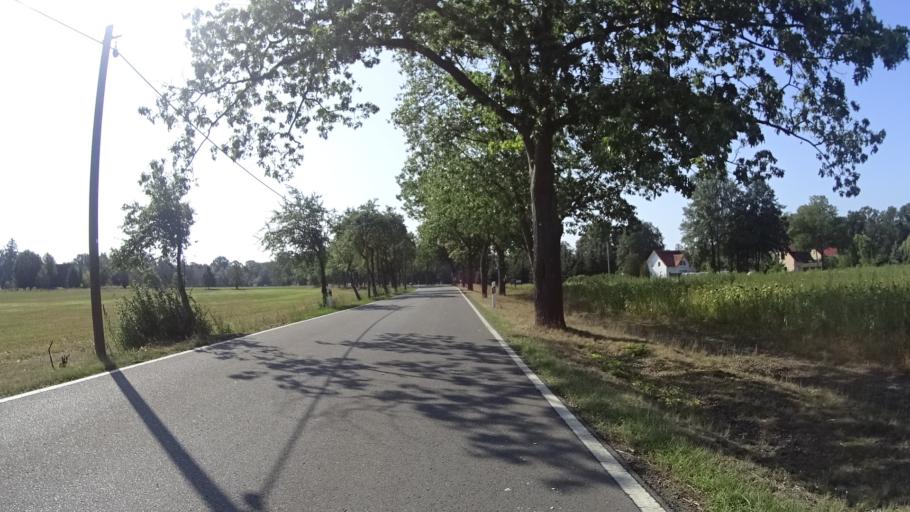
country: DE
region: Brandenburg
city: Burg
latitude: 51.8532
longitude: 14.1344
